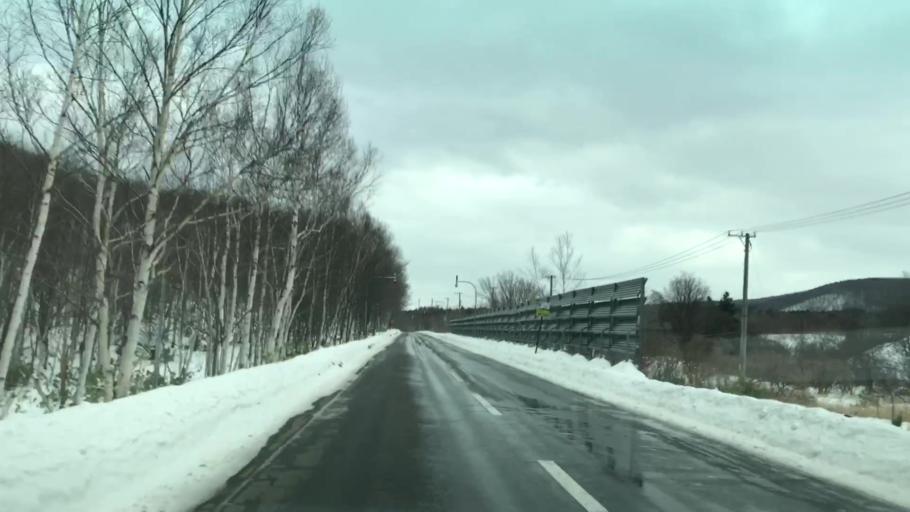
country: JP
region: Hokkaido
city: Yoichi
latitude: 43.3239
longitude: 140.5137
